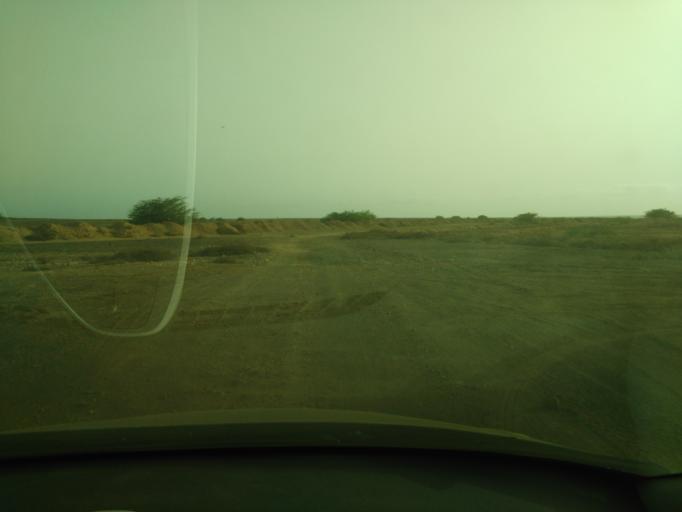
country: CV
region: Sal
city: Santa Maria
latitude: 16.6632
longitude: -22.9340
